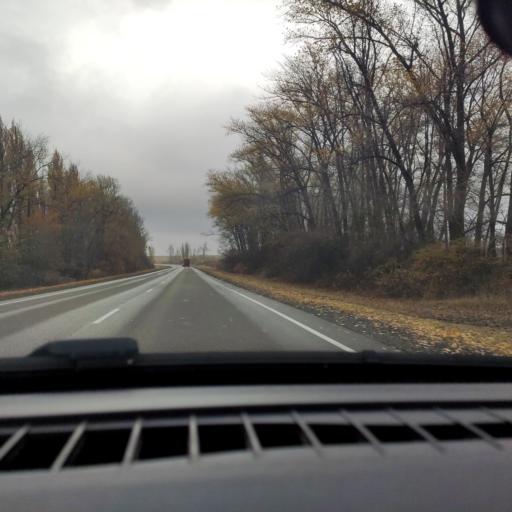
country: RU
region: Voronezj
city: Ostrogozhsk
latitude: 50.9995
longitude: 39.0008
